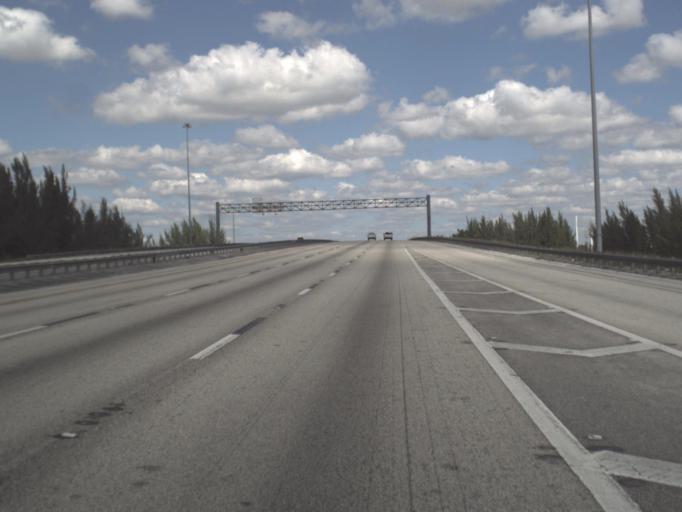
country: US
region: Florida
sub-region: Miami-Dade County
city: Doral
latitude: 25.8734
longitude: -80.3880
